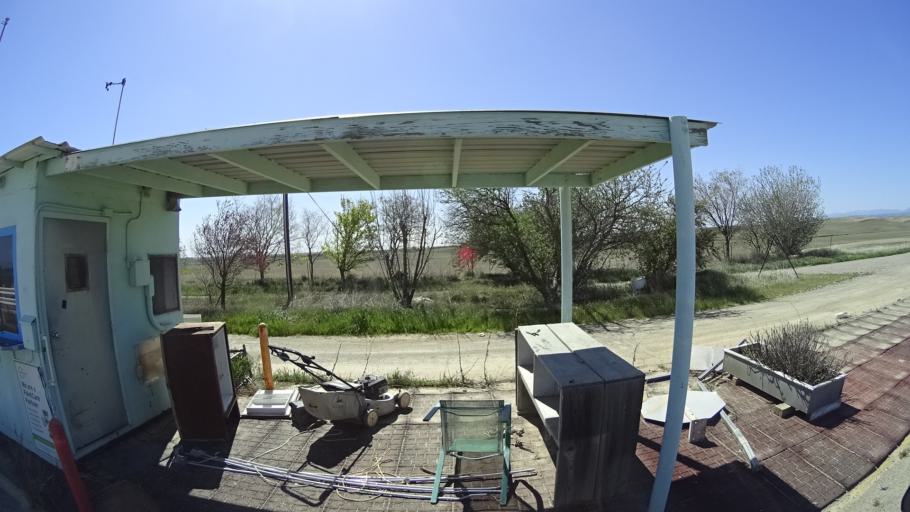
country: US
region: California
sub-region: Glenn County
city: Willows
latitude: 39.6329
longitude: -122.2806
